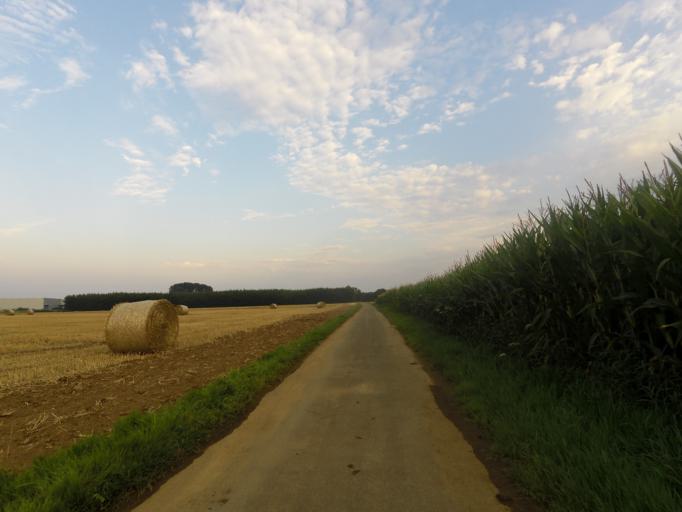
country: NL
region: Gelderland
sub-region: Oude IJsselstreek
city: Gendringen
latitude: 51.8504
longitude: 6.4081
